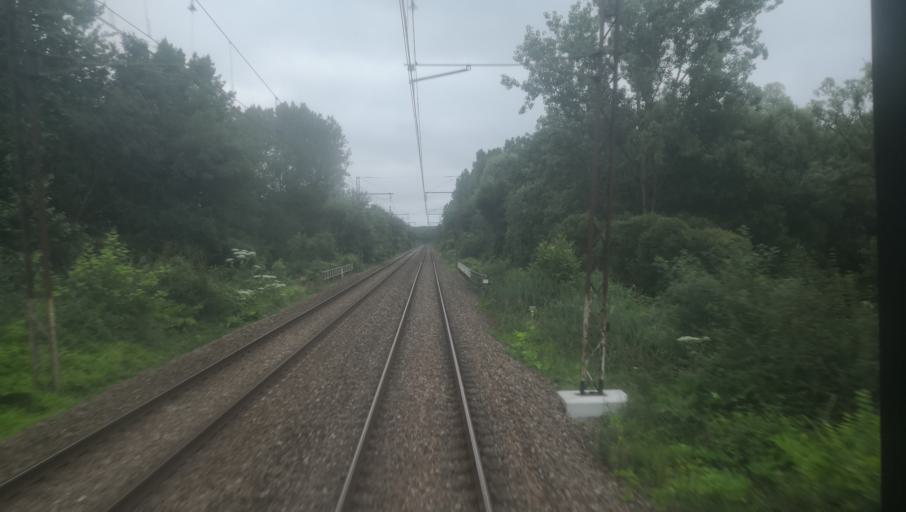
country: FR
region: Centre
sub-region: Departement de l'Indre
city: Reuilly
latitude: 47.0668
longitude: 2.0439
